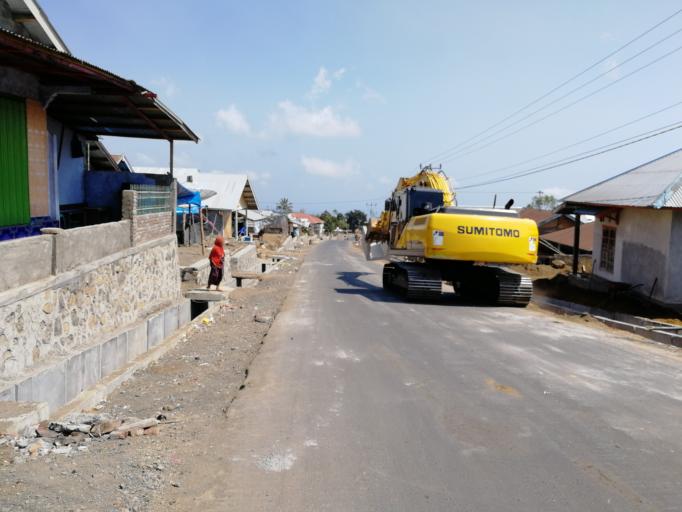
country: ID
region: West Nusa Tenggara
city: Lelongken
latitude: -8.3394
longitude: 116.5007
